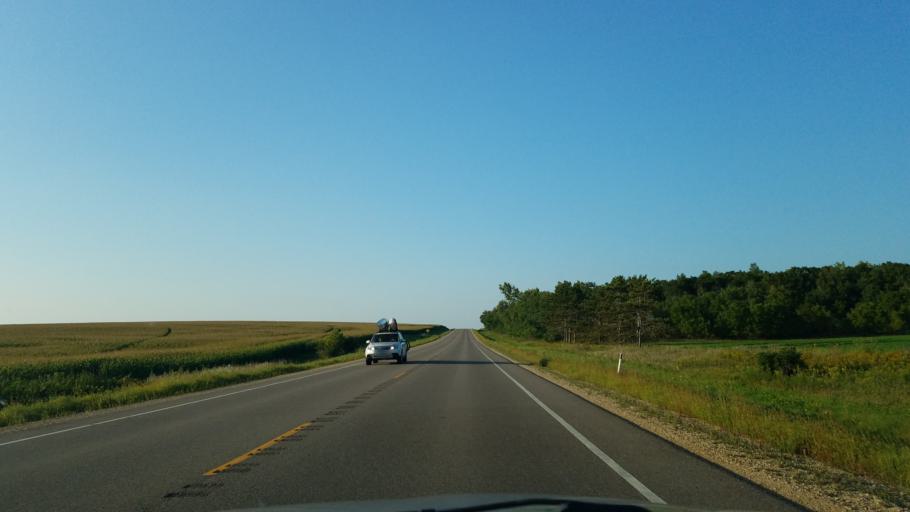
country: US
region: Wisconsin
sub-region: Saint Croix County
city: Baldwin
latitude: 45.0827
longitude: -92.3753
